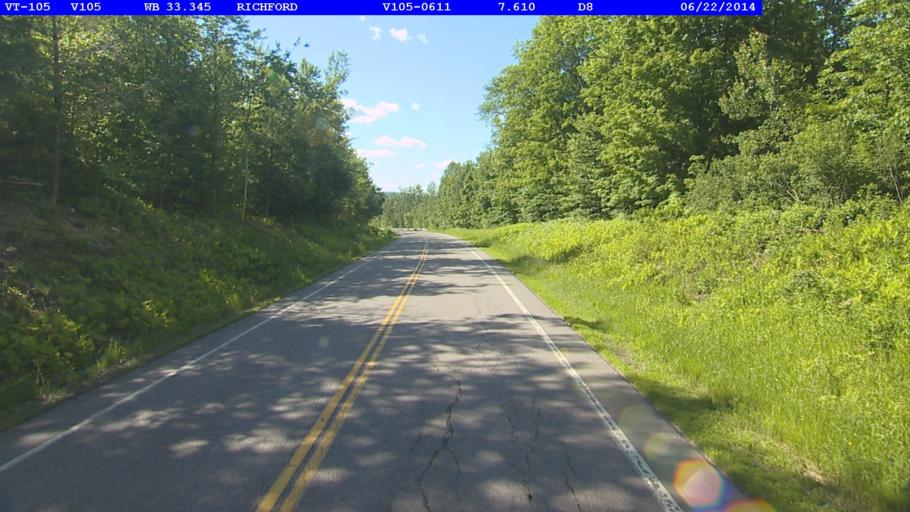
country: US
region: Vermont
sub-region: Franklin County
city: Richford
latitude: 45.0005
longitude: -72.5736
